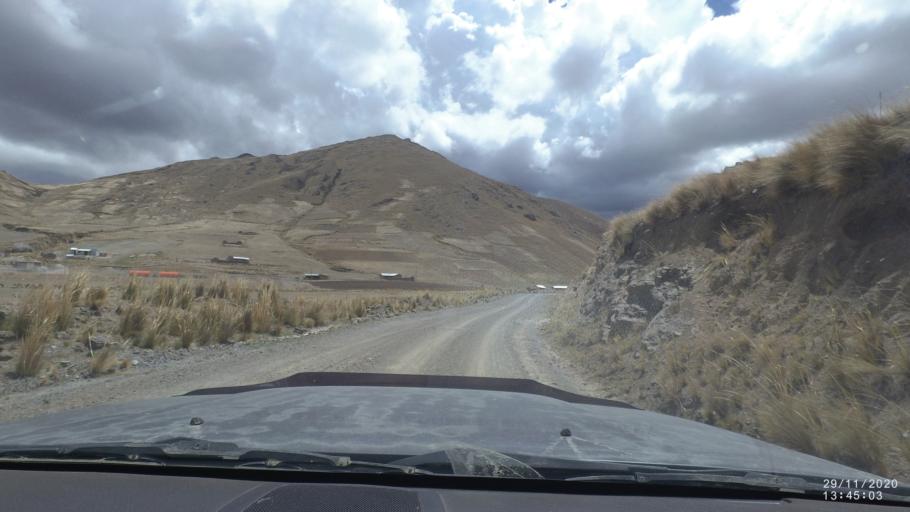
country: BO
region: Cochabamba
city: Cochabamba
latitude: -17.1480
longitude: -66.3188
